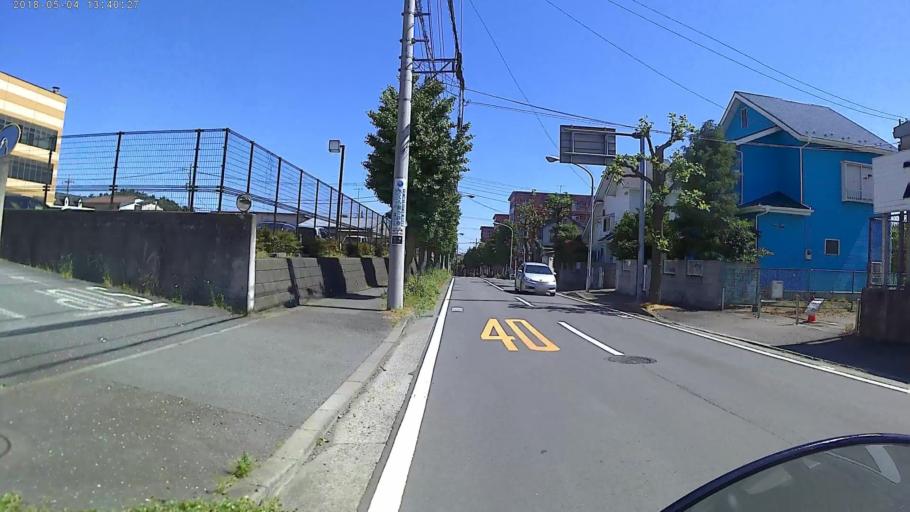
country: JP
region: Kanagawa
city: Minami-rinkan
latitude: 35.4428
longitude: 139.4549
